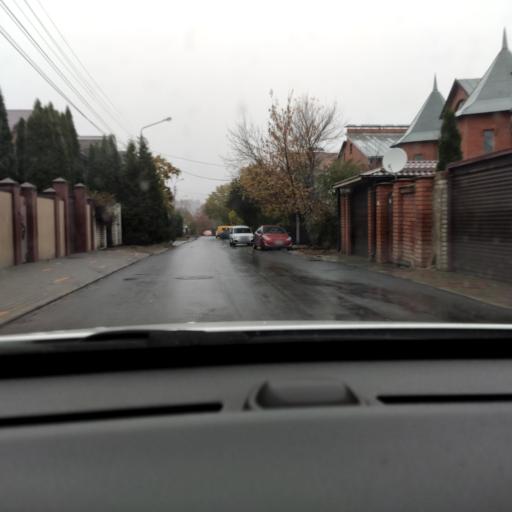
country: RU
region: Voronezj
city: Voronezh
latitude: 51.7066
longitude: 39.2028
